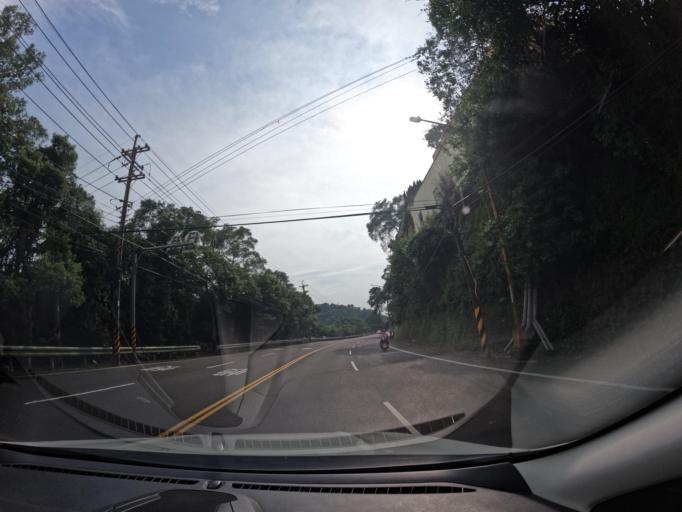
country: TW
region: Taiwan
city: Daxi
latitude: 24.8937
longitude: 121.3078
